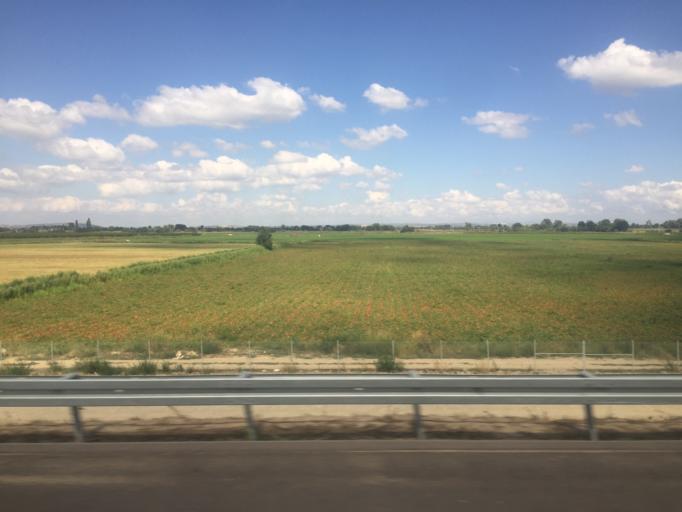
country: TR
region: Bursa
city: Tatkavakli
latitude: 40.0785
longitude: 28.2574
